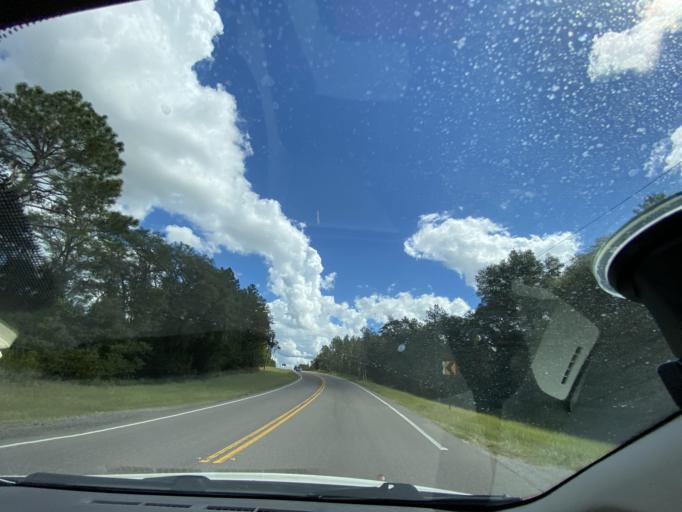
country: US
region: Florida
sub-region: Citrus County
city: Hernando
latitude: 29.0264
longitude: -82.2500
